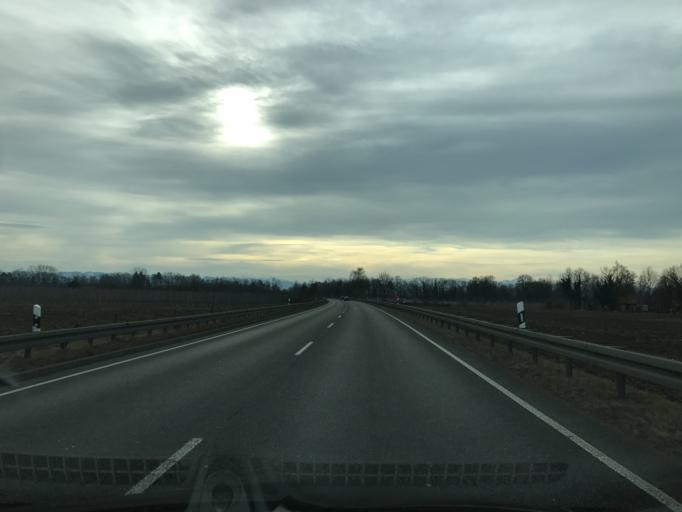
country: DE
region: Baden-Wuerttemberg
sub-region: Tuebingen Region
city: Kressbronn am Bodensee
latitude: 47.6124
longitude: 9.5713
